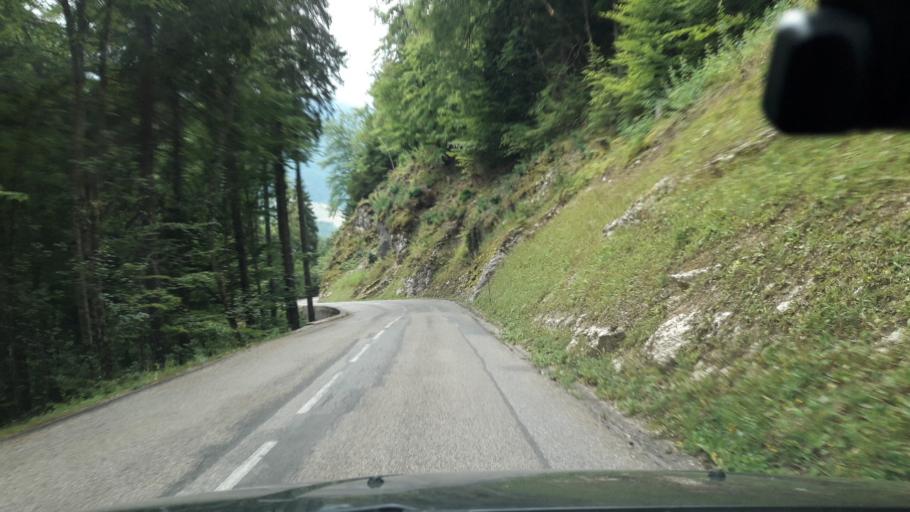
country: FR
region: Rhone-Alpes
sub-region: Departement de la Savoie
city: Vimines
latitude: 45.4541
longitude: 5.8686
